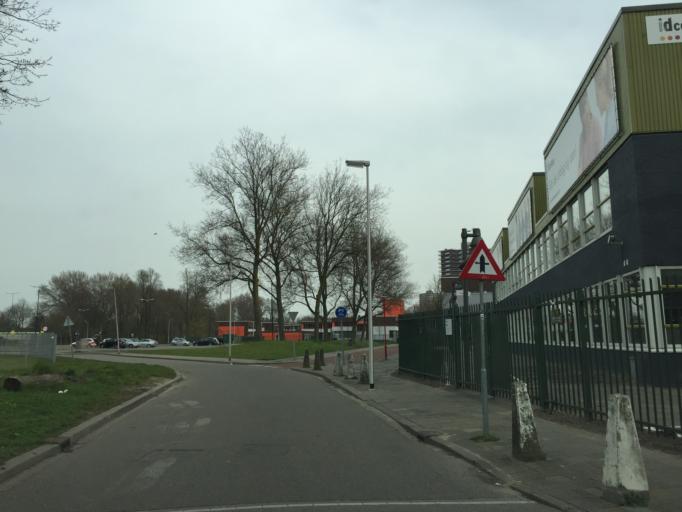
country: NL
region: South Holland
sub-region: Gemeente Zoetermeer
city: Zoetermeer
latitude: 52.0613
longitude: 4.5022
